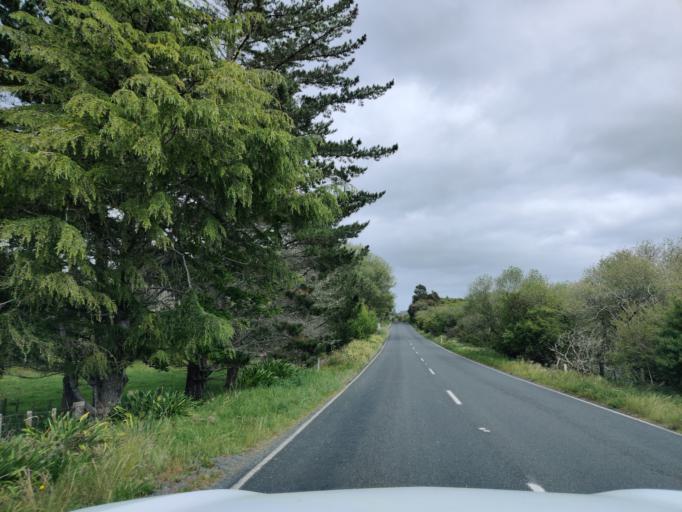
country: NZ
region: Waikato
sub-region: Waikato District
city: Ngaruawahia
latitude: -37.5775
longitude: 175.1306
